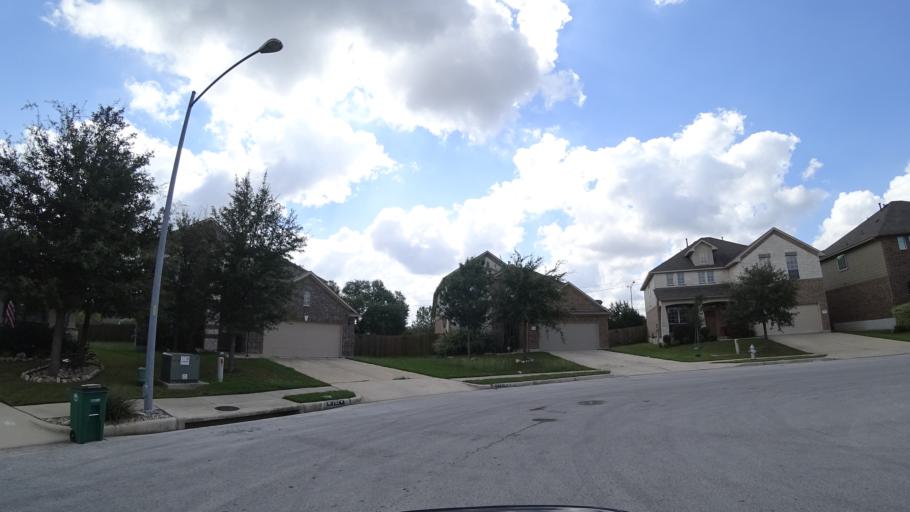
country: US
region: Texas
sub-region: Travis County
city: Onion Creek
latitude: 30.1861
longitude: -97.7976
